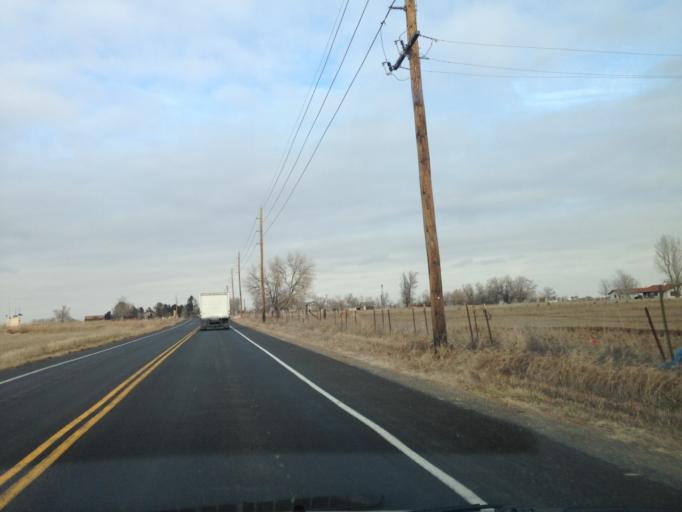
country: US
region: Colorado
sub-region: Boulder County
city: Lafayette
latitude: 40.0025
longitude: -105.0745
